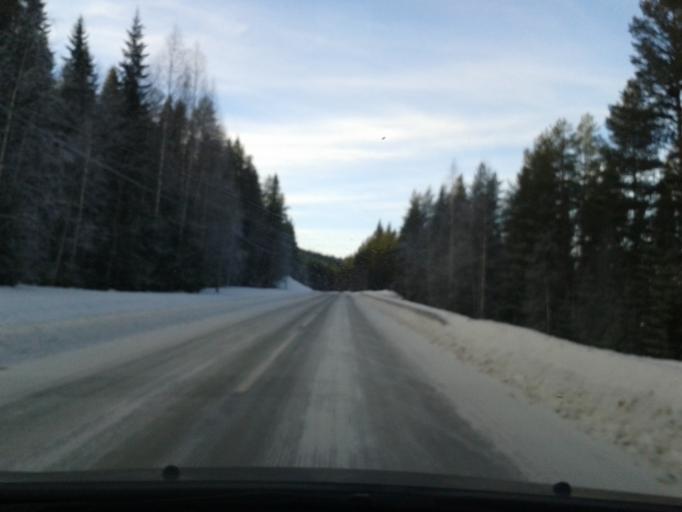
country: SE
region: Vaesternorrland
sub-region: OErnskoeldsviks Kommun
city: Bredbyn
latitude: 63.6616
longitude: 17.8482
